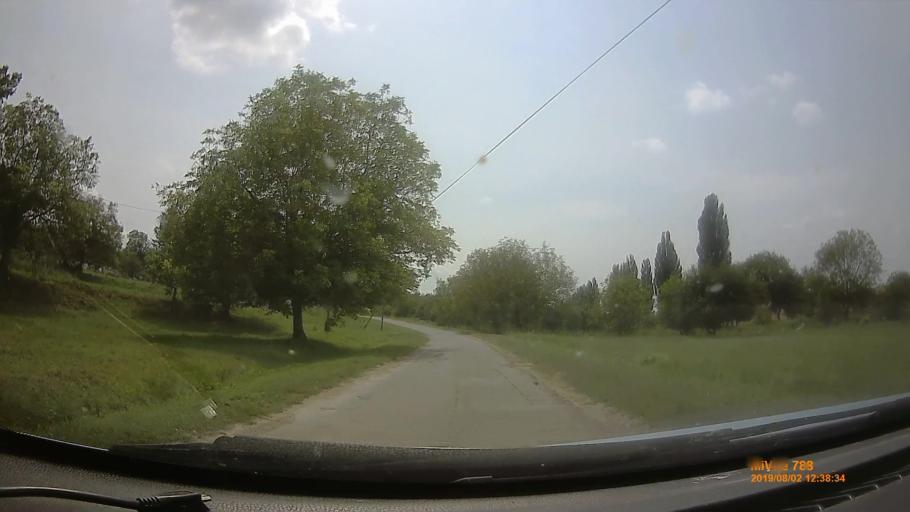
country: HU
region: Baranya
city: Buekkoesd
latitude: 46.0952
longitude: 17.9571
